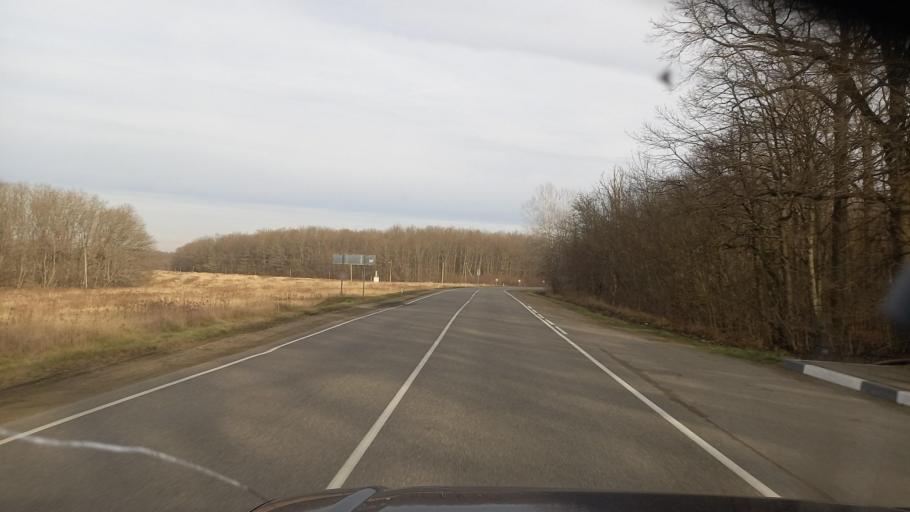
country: RU
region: Krasnodarskiy
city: Khadyzhensk
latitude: 44.6367
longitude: 39.5095
